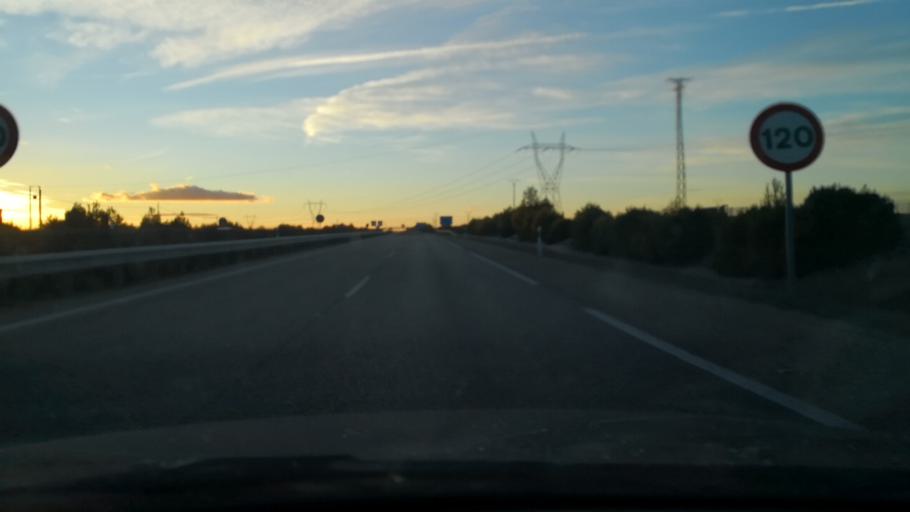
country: ES
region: Castille and Leon
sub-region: Provincia de Valladolid
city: Tordesillas
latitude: 41.5040
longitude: -5.0274
